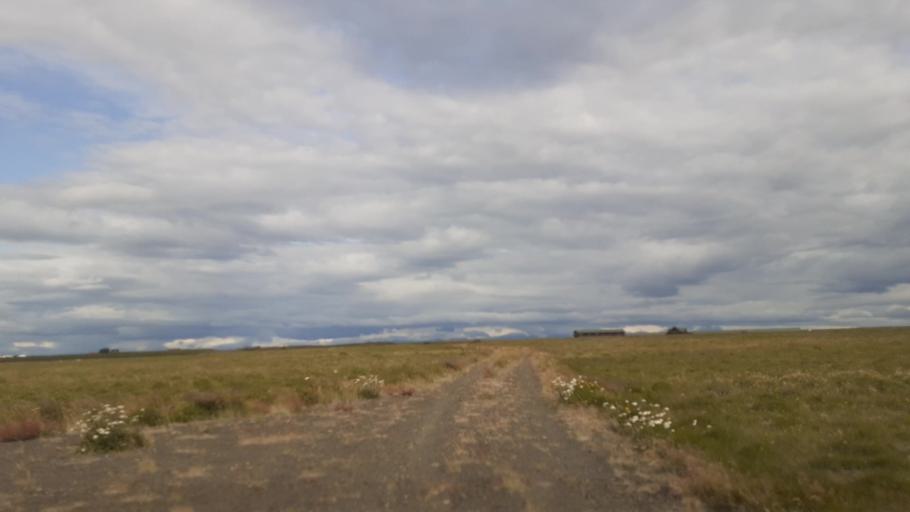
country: IS
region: South
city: Vestmannaeyjar
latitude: 63.7752
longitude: -20.3004
